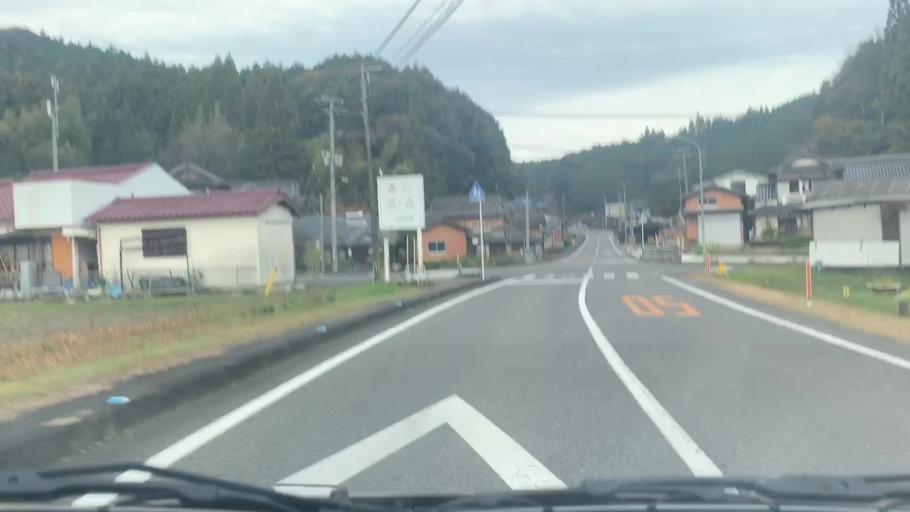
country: JP
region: Saga Prefecture
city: Ureshinomachi-shimojuku
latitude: 33.1271
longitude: 129.9804
